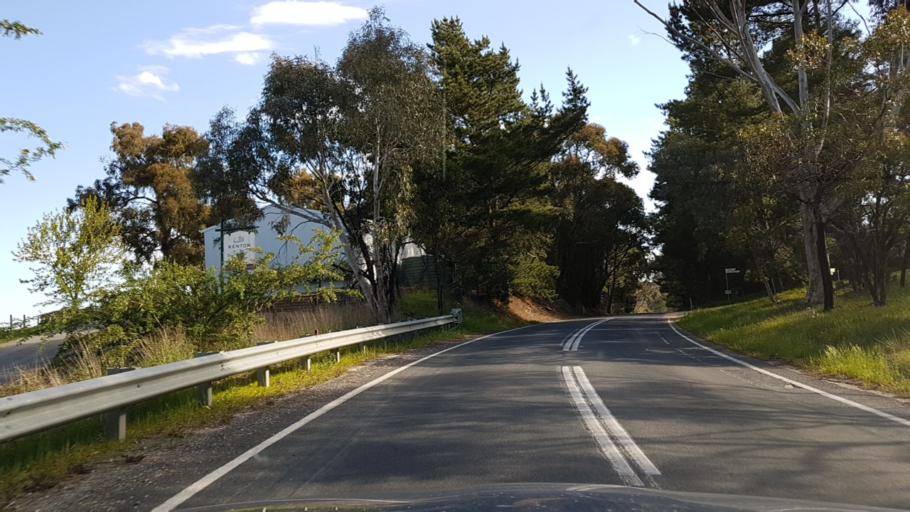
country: AU
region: South Australia
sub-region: Adelaide Hills
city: Lobethal
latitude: -34.8787
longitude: 138.8919
